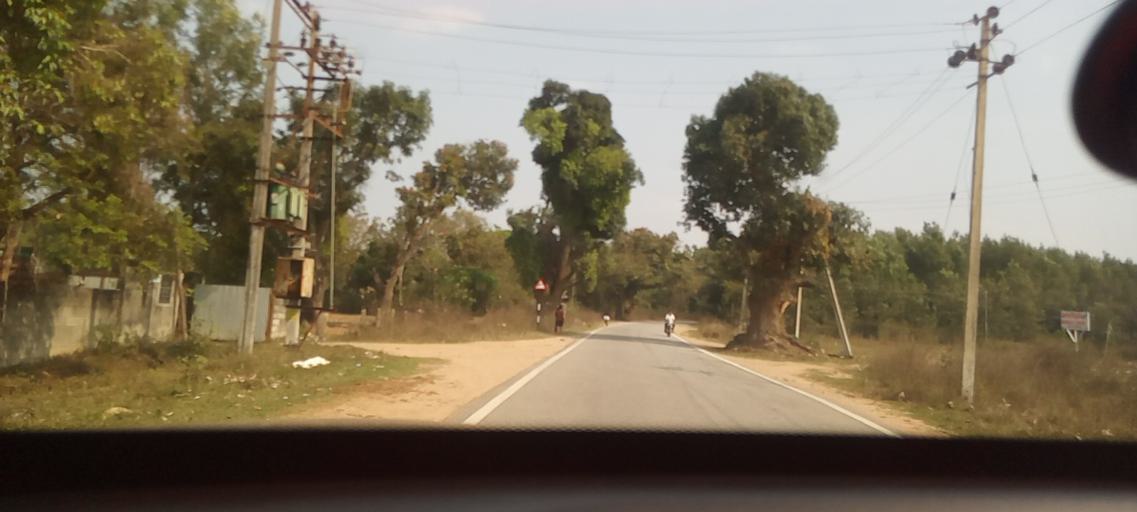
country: IN
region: Karnataka
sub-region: Hassan
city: Belur
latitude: 13.1873
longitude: 75.7986
